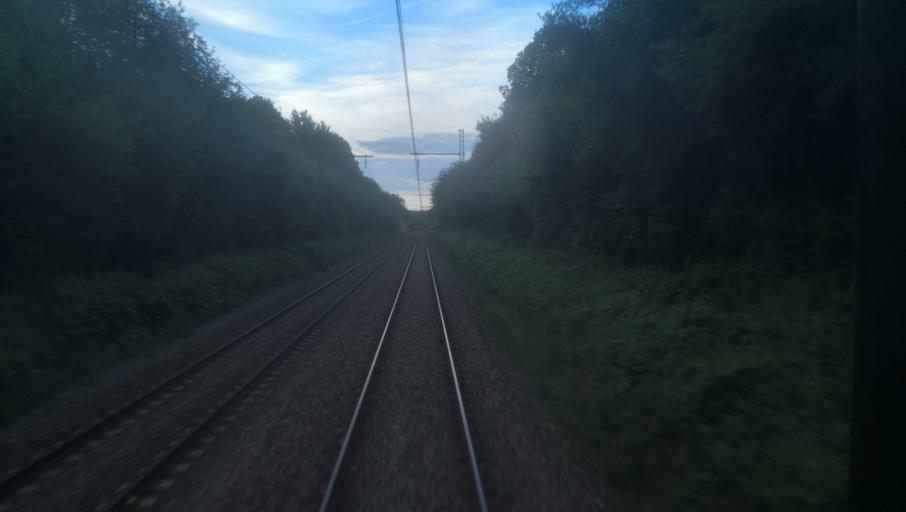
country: FR
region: Limousin
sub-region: Departement de la Creuse
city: Saint-Maurice-la-Souterraine
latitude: 46.1942
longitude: 1.4682
